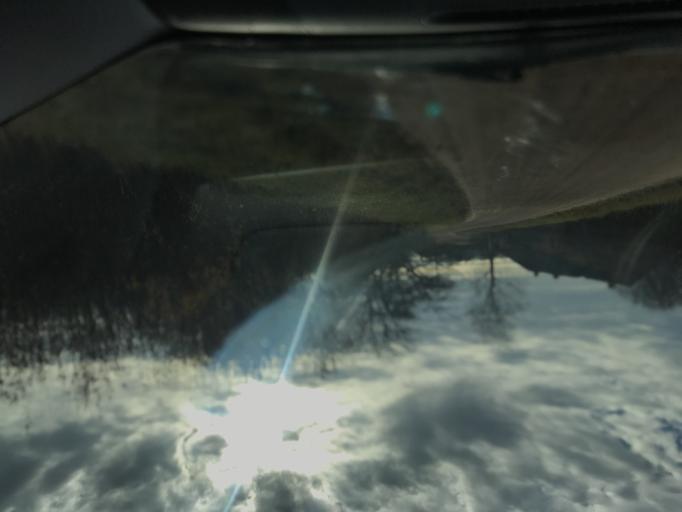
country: BY
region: Vitebsk
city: Haradok
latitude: 55.4535
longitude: 30.0350
